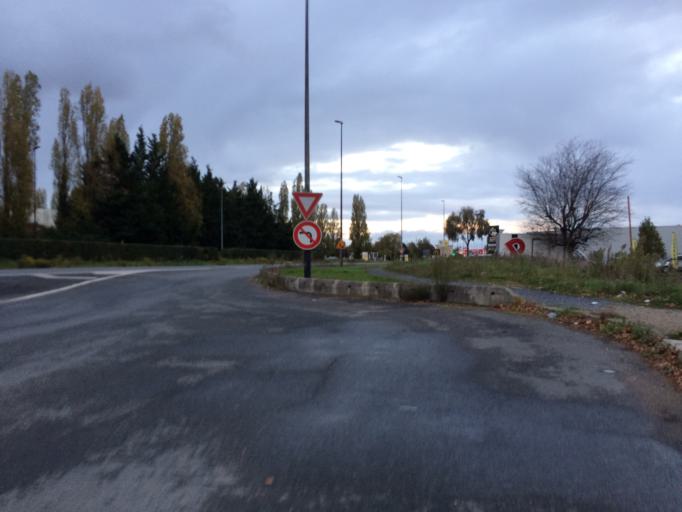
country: FR
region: Ile-de-France
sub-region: Departement de l'Essonne
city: Orsay
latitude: 48.6778
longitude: 2.1991
